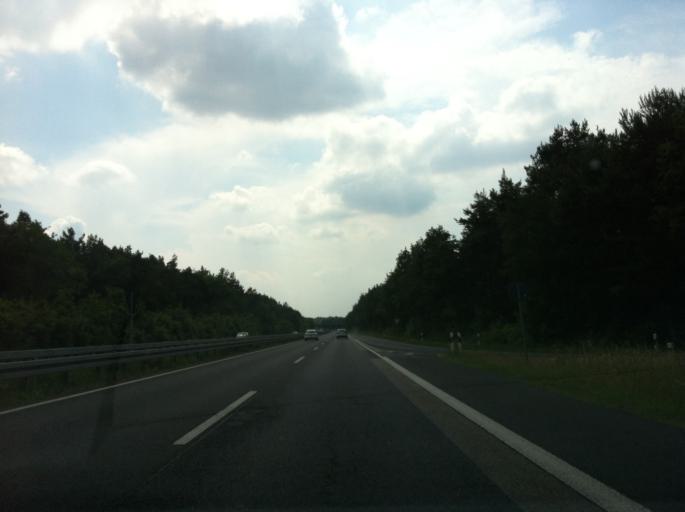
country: DE
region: Hesse
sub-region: Regierungsbezirk Darmstadt
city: Rodgau
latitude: 49.9968
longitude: 8.8885
